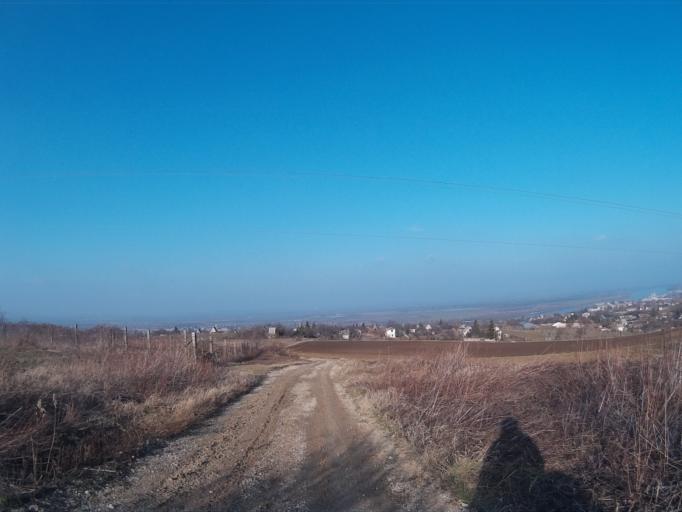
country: HU
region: Komarom-Esztergom
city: Labatlan
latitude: 47.7396
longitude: 18.4823
